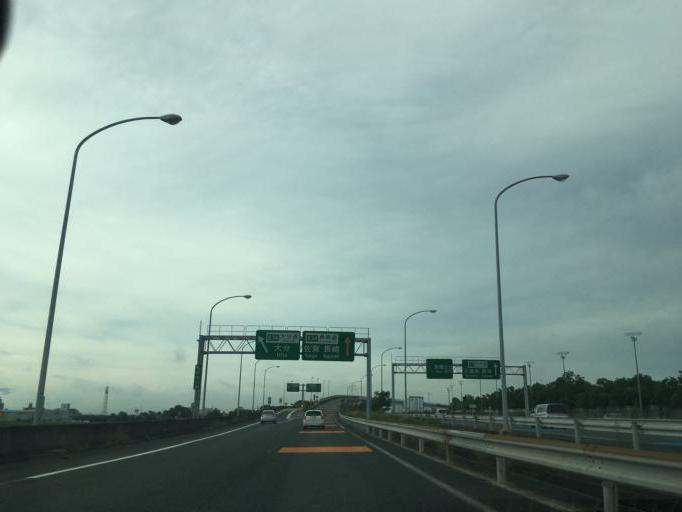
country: JP
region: Saga Prefecture
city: Tosu
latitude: 33.4025
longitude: 130.5383
